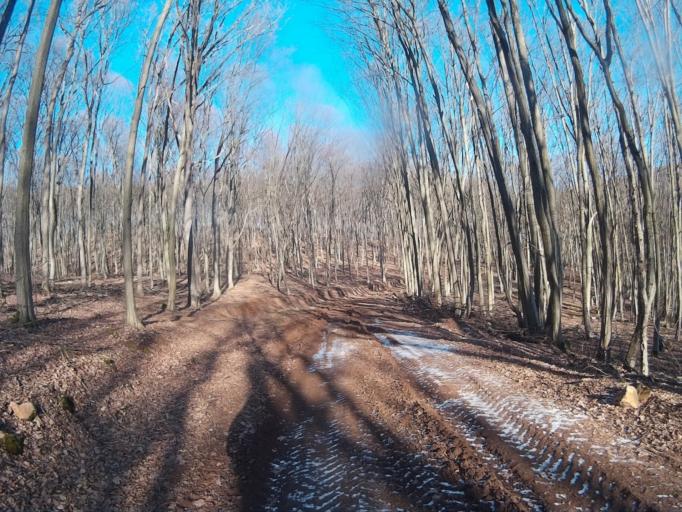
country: HU
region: Borsod-Abauj-Zemplen
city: Rudabanya
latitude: 48.5043
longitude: 20.6024
